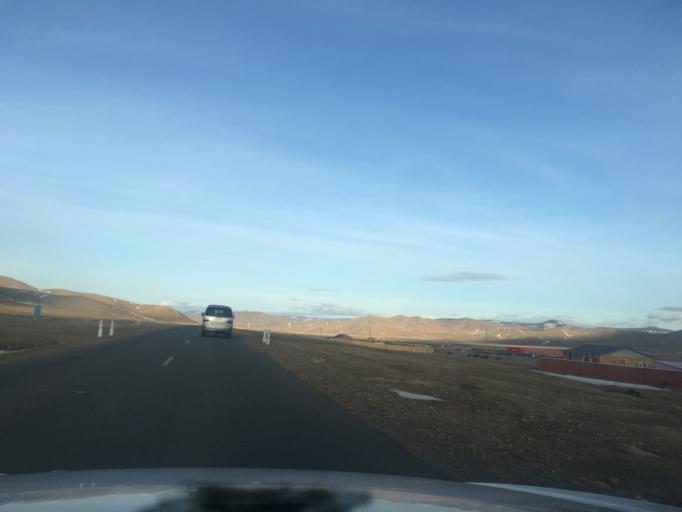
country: MN
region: Central Aimak
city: Mandal
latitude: 48.0996
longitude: 106.6181
